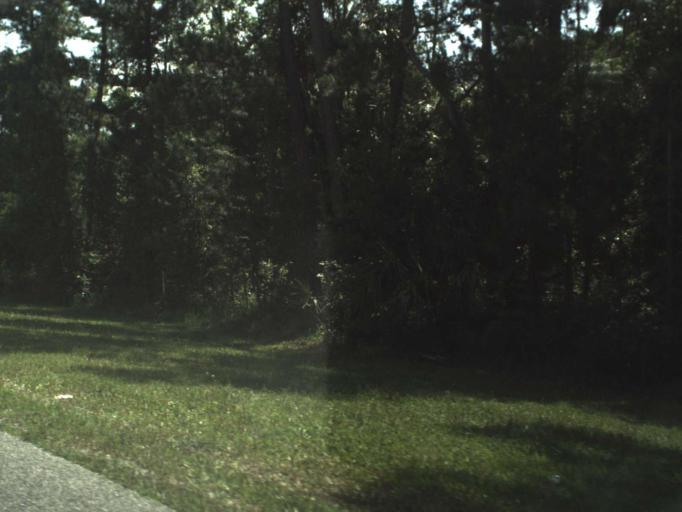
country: US
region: Florida
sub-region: Volusia County
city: Daytona Beach
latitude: 29.1565
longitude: -81.1012
